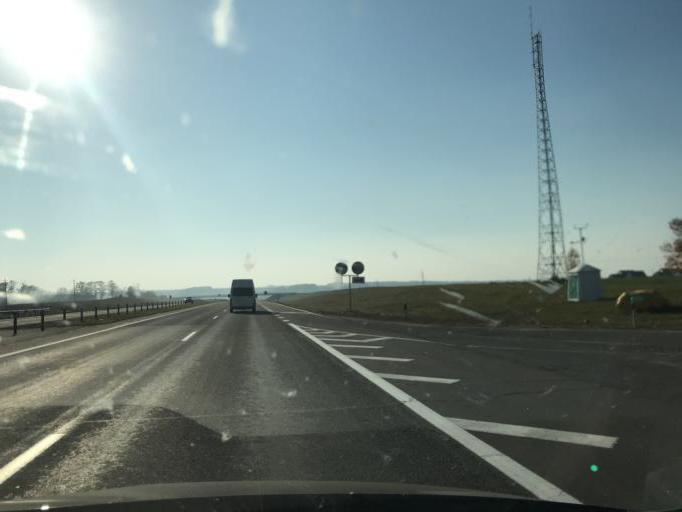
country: BY
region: Minsk
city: Haradzyeya
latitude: 53.3483
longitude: 26.4536
